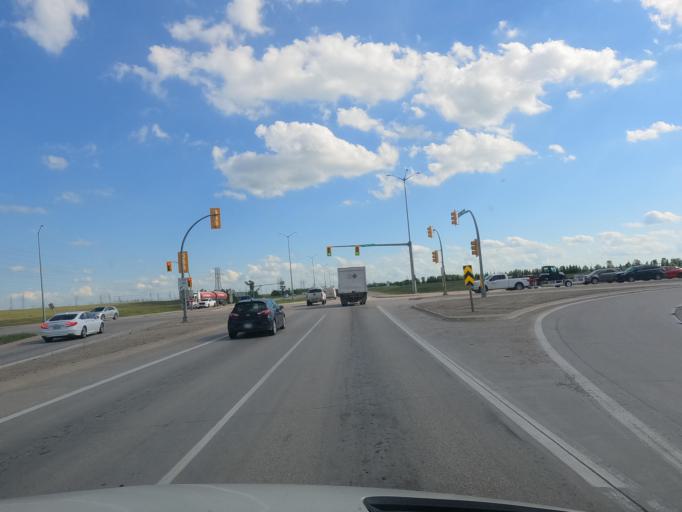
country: CA
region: Manitoba
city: Winnipeg
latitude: 49.8863
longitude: -96.9596
